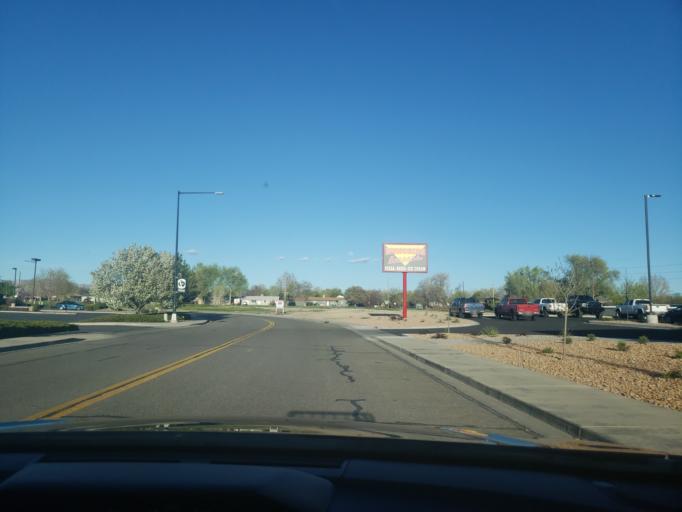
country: US
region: Colorado
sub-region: Mesa County
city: Fruita
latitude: 39.1505
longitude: -108.7364
